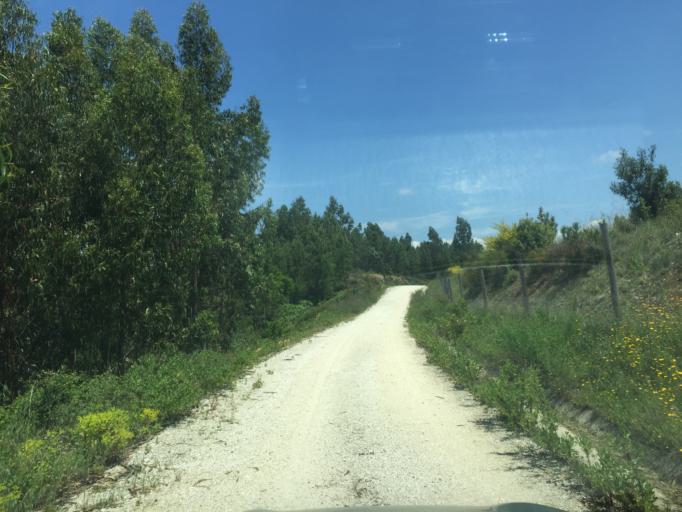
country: PT
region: Castelo Branco
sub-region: Serta
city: Serta
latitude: 39.8407
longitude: -8.0637
